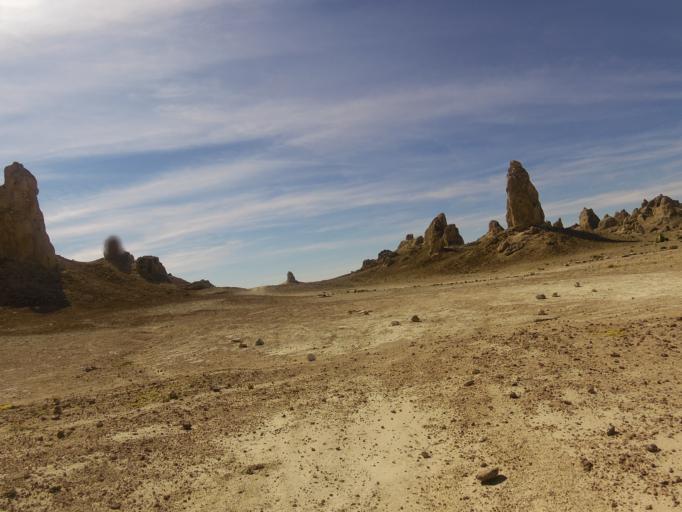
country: US
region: California
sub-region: San Bernardino County
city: Searles Valley
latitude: 35.6186
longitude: -117.3689
